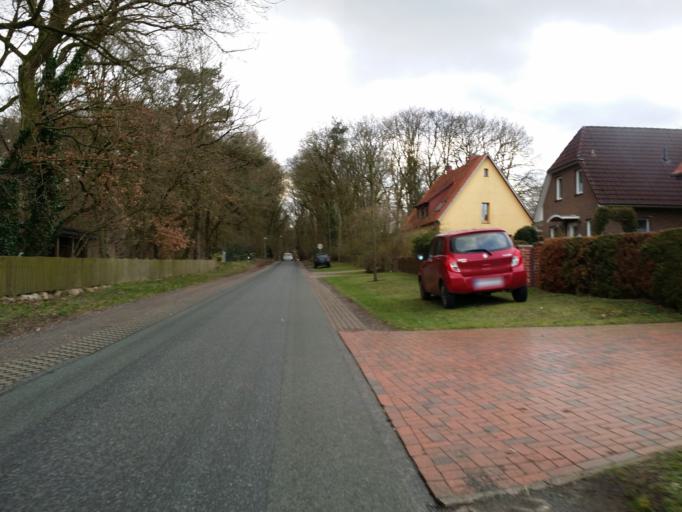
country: DE
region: Lower Saxony
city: Gross Ippener
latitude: 52.9693
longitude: 8.6267
